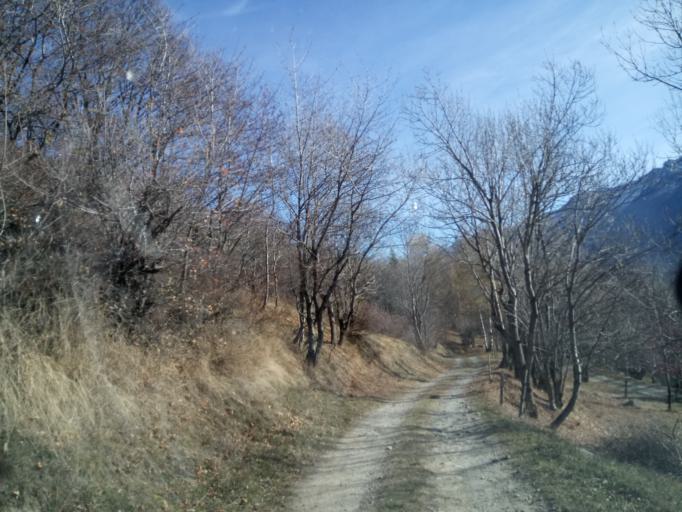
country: FR
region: Rhone-Alpes
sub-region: Departement de la Savoie
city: Saint-Michel-de-Maurienne
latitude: 45.2277
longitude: 6.4911
